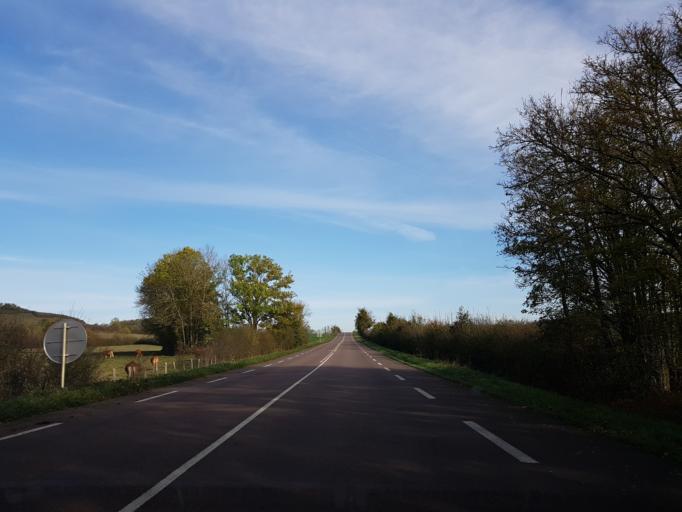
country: FR
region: Bourgogne
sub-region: Departement de la Cote-d'Or
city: Vitteaux
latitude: 47.3927
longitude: 4.4489
